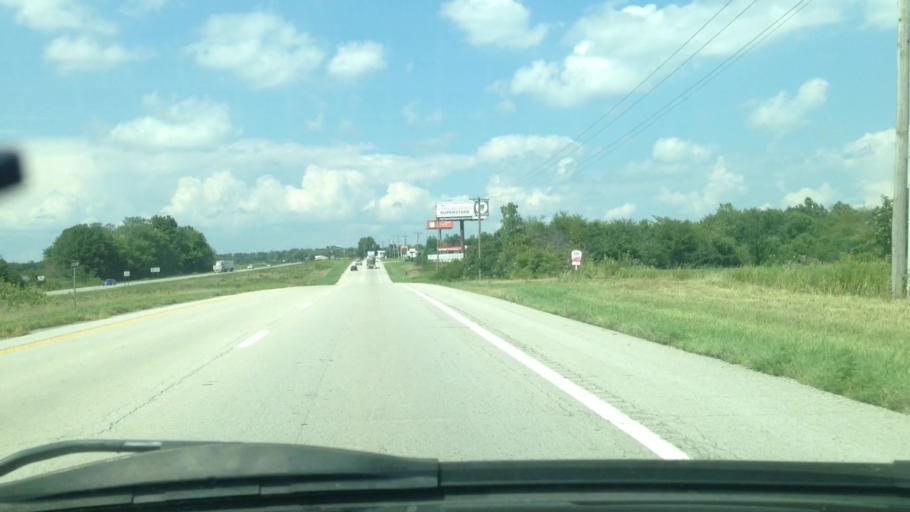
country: US
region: Missouri
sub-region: Lincoln County
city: Troy
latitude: 39.1313
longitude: -90.9641
